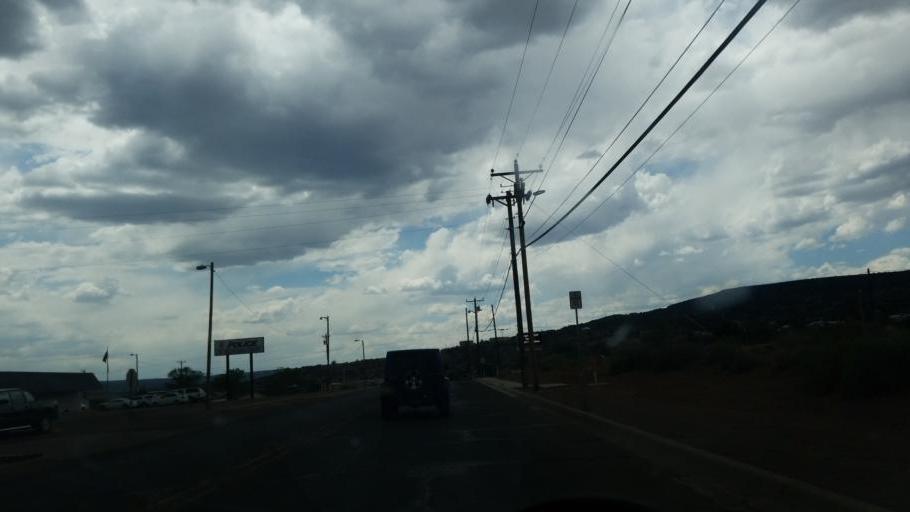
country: US
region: New Mexico
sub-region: Cibola County
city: Grants
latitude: 35.1612
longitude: -107.8387
